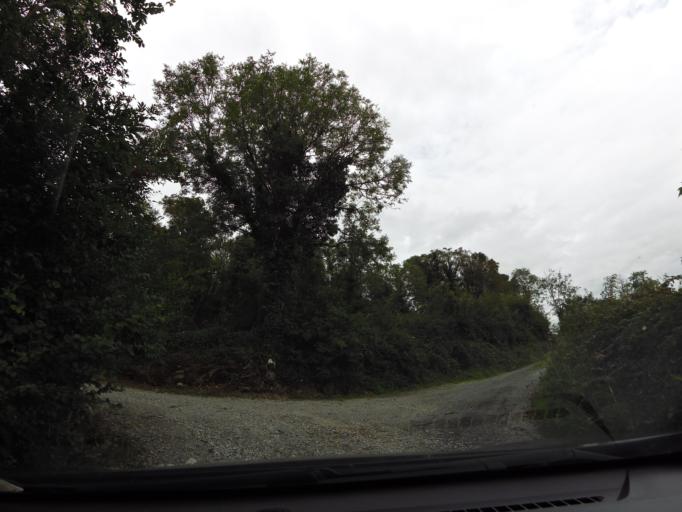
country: IE
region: Connaught
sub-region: County Galway
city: Loughrea
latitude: 53.1585
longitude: -8.4406
